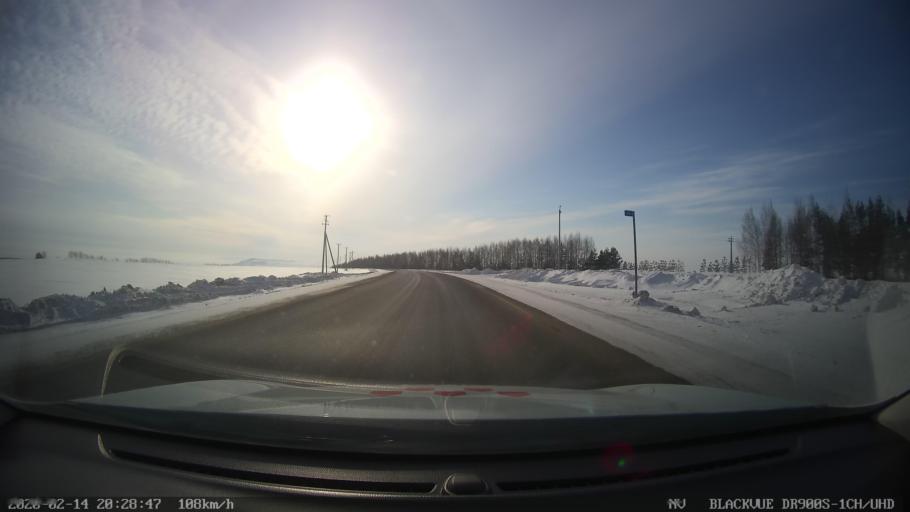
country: RU
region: Tatarstan
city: Stolbishchi
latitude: 55.4581
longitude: 48.9774
